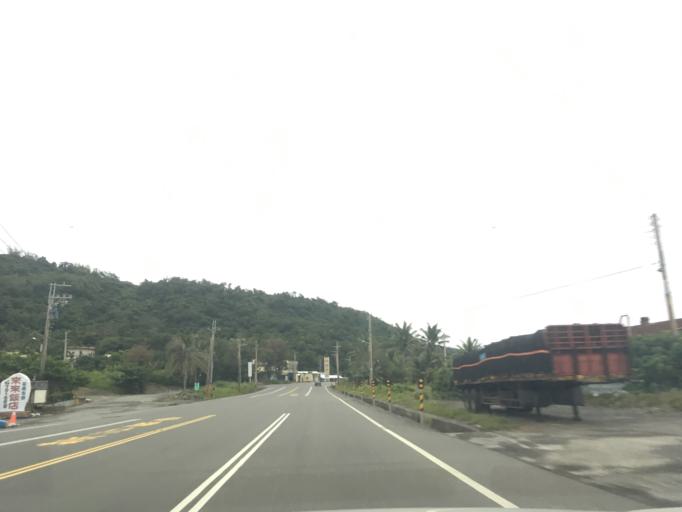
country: TW
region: Taiwan
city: Hengchun
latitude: 22.3286
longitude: 120.8922
